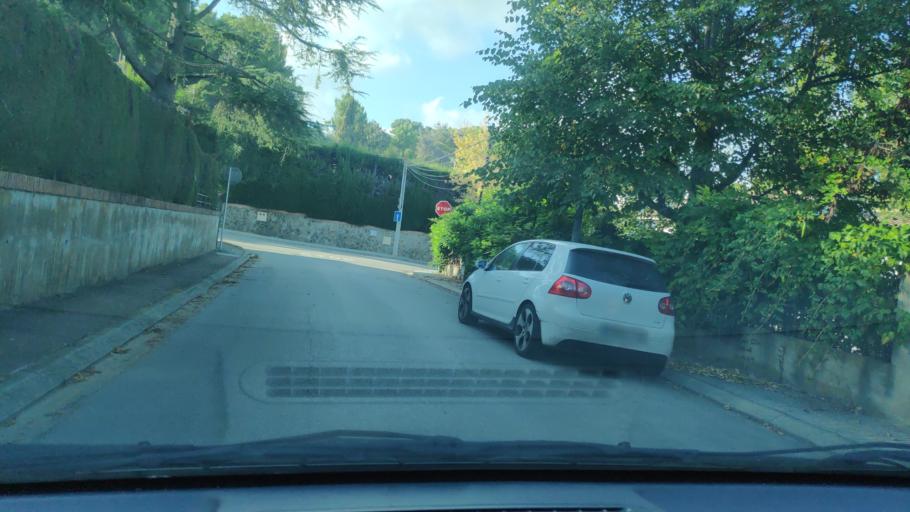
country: ES
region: Catalonia
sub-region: Provincia de Barcelona
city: Sant Quirze del Valles
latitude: 41.5071
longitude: 2.0919
